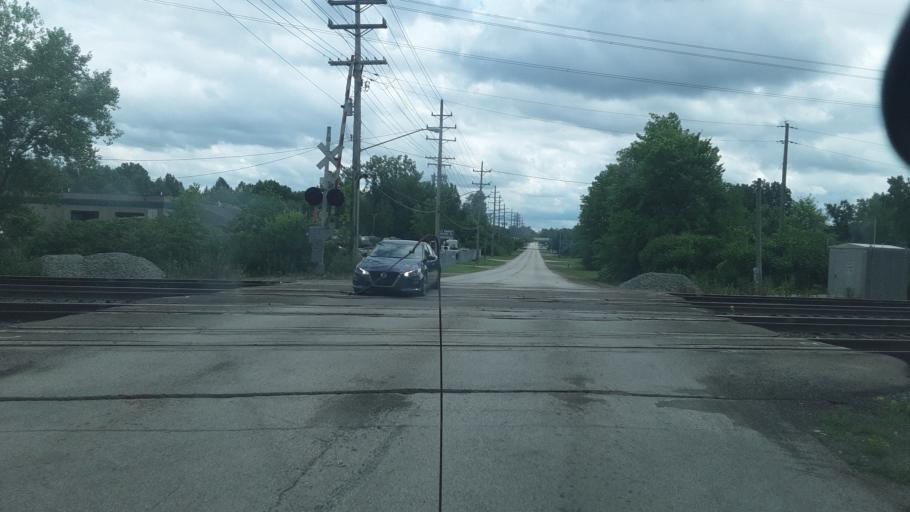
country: US
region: Ohio
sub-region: Ashtabula County
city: Edgewood
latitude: 41.8859
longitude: -80.7725
